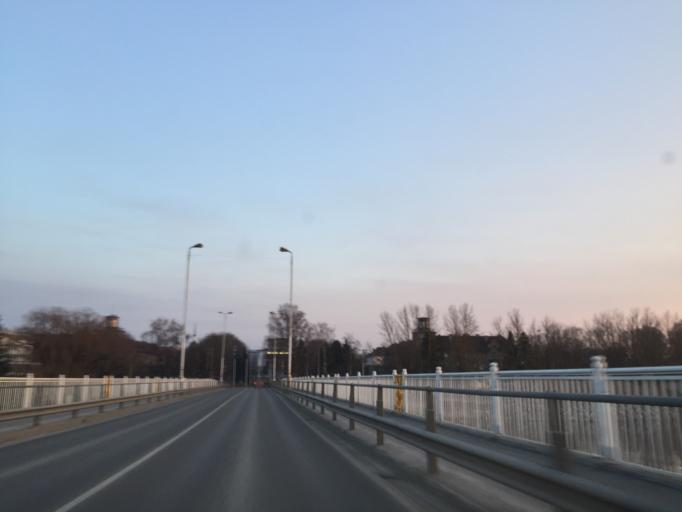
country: EE
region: Paernumaa
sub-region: Paernu linn
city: Parnu
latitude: 58.3888
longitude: 24.4959
